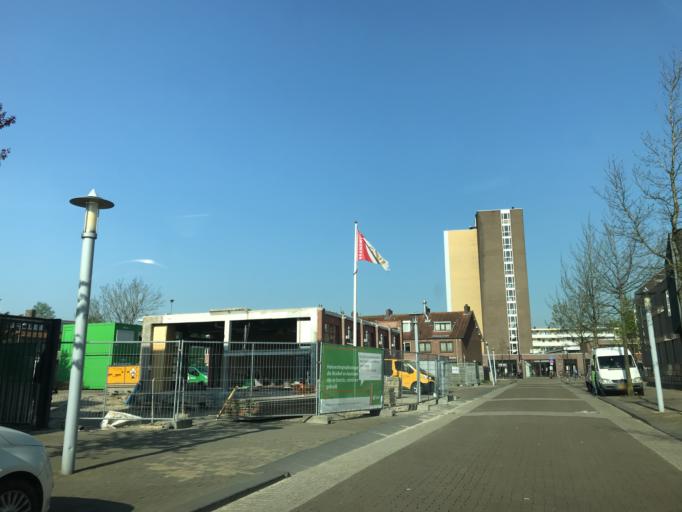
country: NL
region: North Holland
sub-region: Gemeente Diemen
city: Diemen
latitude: 52.3411
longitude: 4.9650
